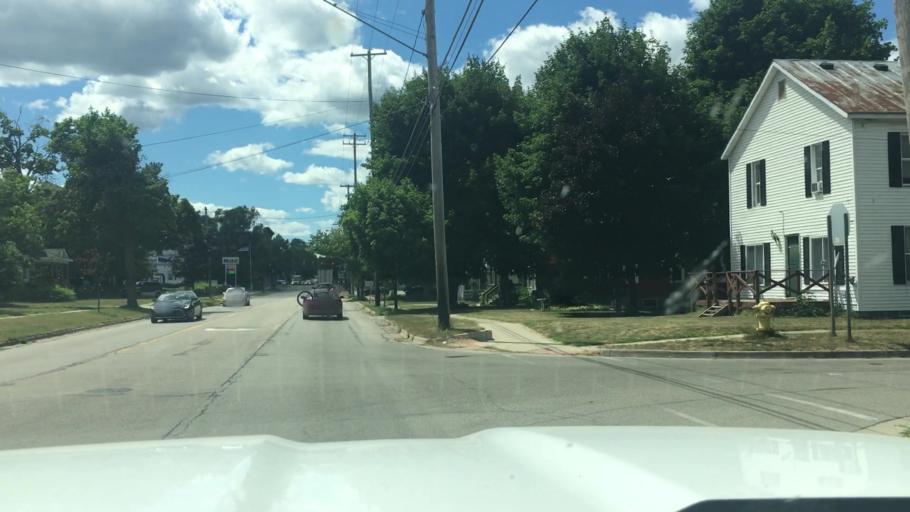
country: US
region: Michigan
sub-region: Montcalm County
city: Greenville
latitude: 43.1775
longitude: -85.2502
